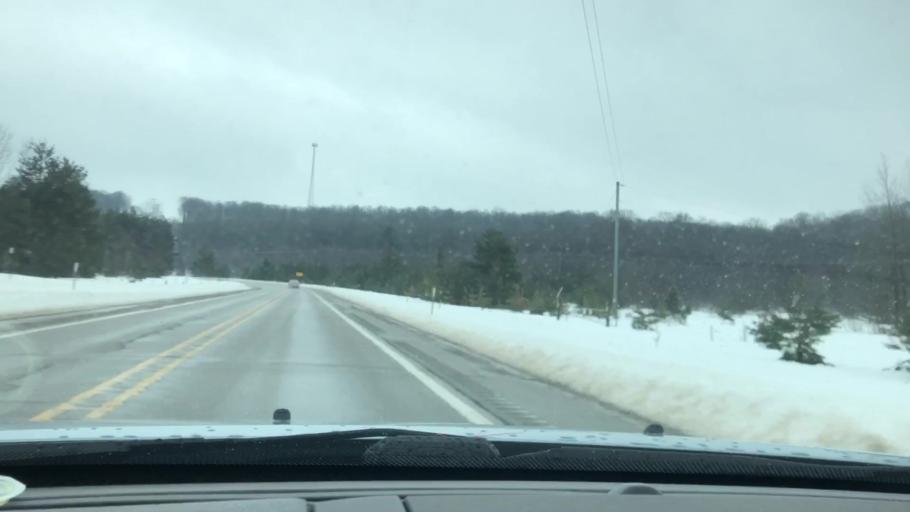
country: US
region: Michigan
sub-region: Charlevoix County
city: Boyne City
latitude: 45.0830
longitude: -84.9230
